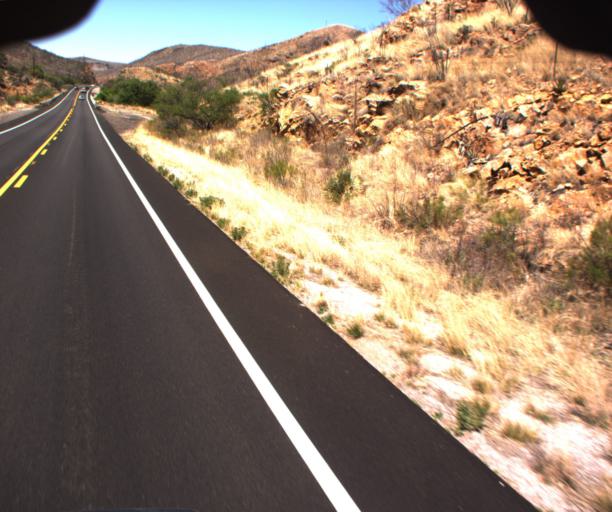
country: US
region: Arizona
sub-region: Cochise County
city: Bisbee
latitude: 31.5007
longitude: -110.0039
